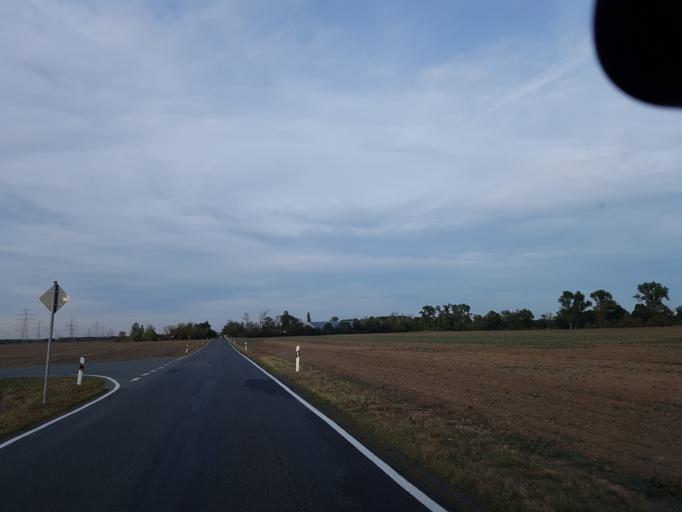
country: DE
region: Saxony
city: Wulknitz
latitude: 51.3496
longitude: 13.3960
